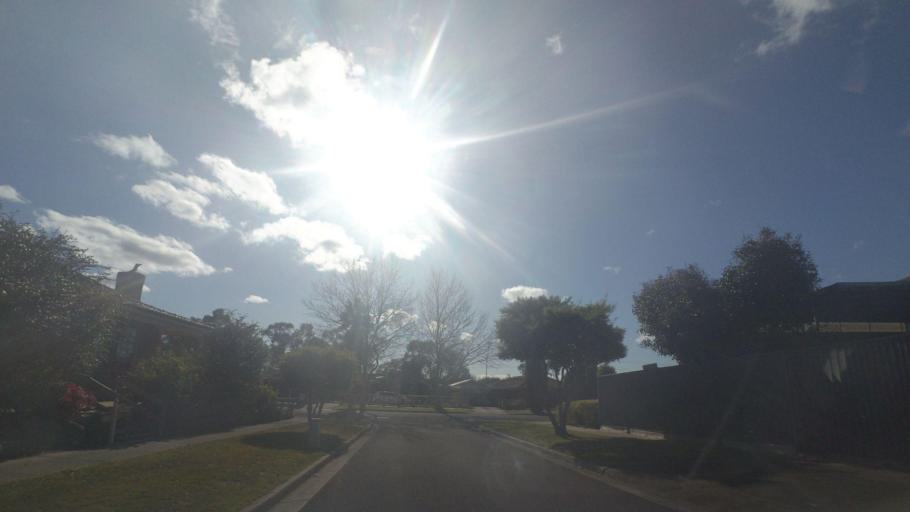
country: AU
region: Victoria
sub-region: Knox
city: Knoxfield
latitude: -37.9138
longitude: 145.2552
